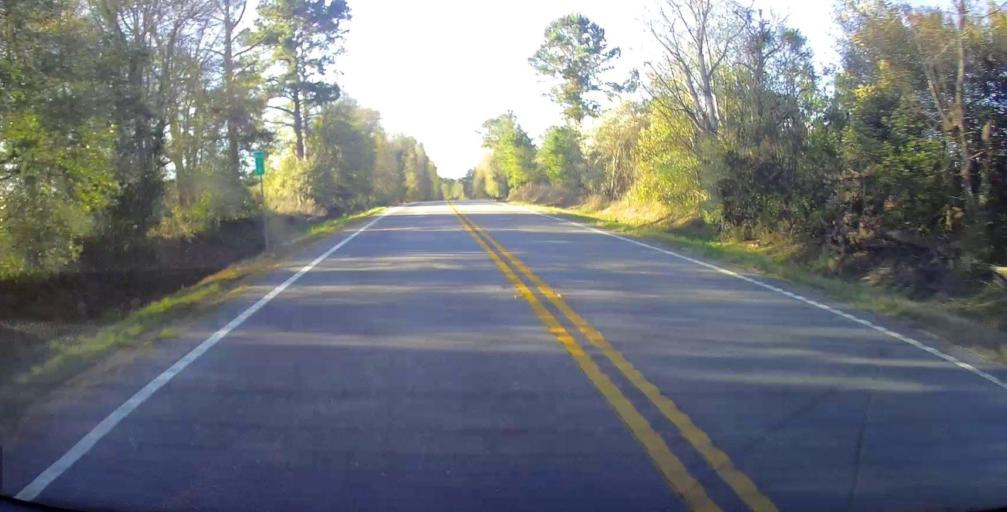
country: US
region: Georgia
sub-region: Pulaski County
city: Hawkinsville
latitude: 32.2322
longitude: -83.3969
